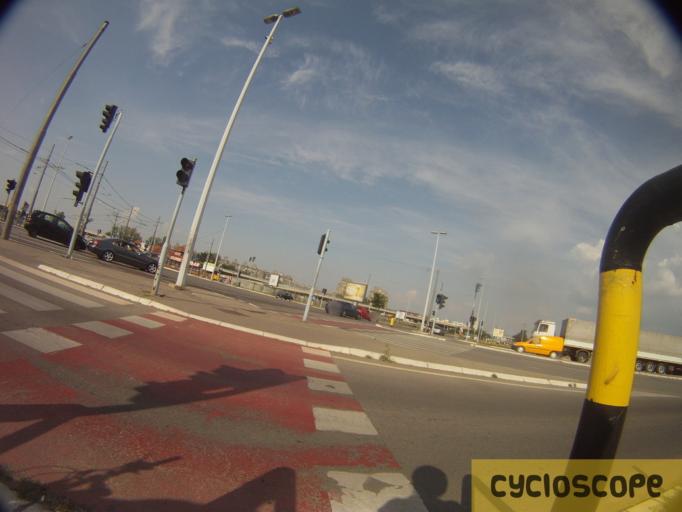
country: RS
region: Central Serbia
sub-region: Belgrade
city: Novi Beograd
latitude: 44.8036
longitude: 20.4171
